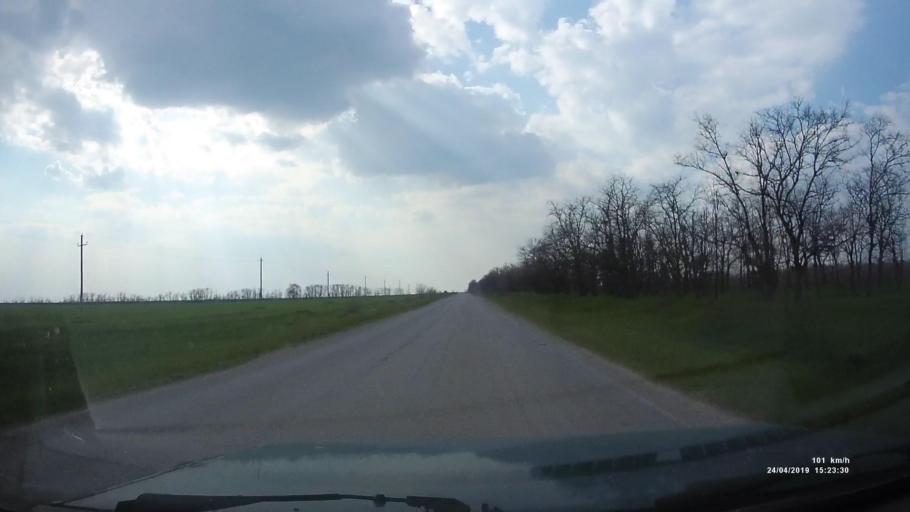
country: RU
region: Rostov
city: Remontnoye
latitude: 46.5436
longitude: 43.0887
